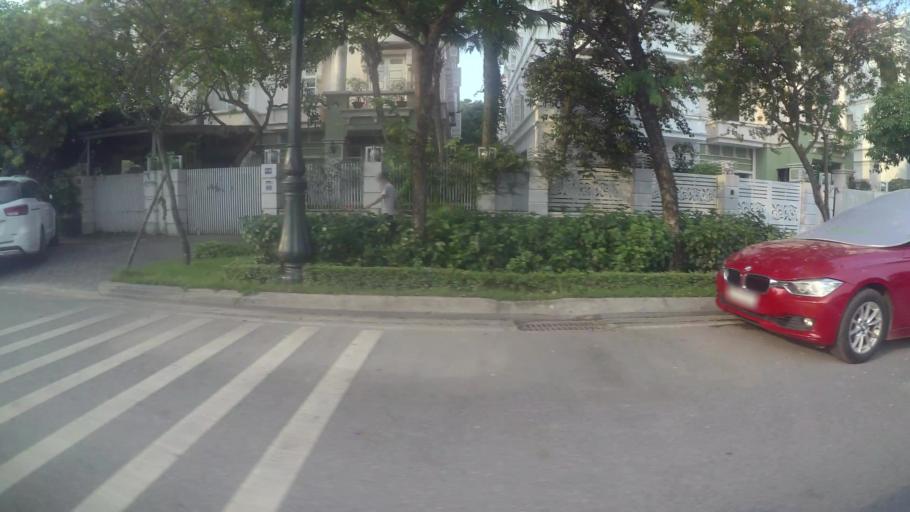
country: VN
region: Ha Noi
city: Tay Ho
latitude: 21.0756
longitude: 105.7993
